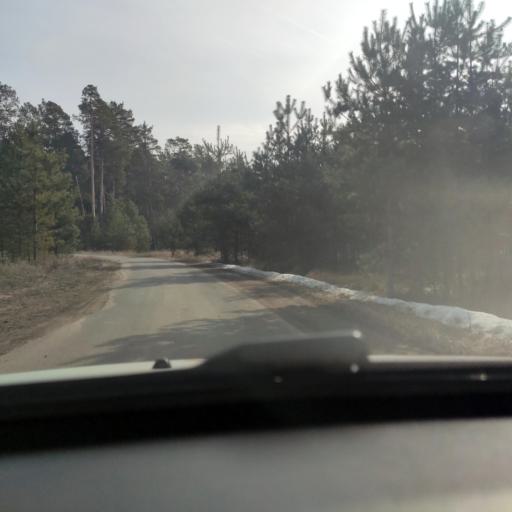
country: RU
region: Voronezj
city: Ramon'
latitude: 51.8908
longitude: 39.3675
